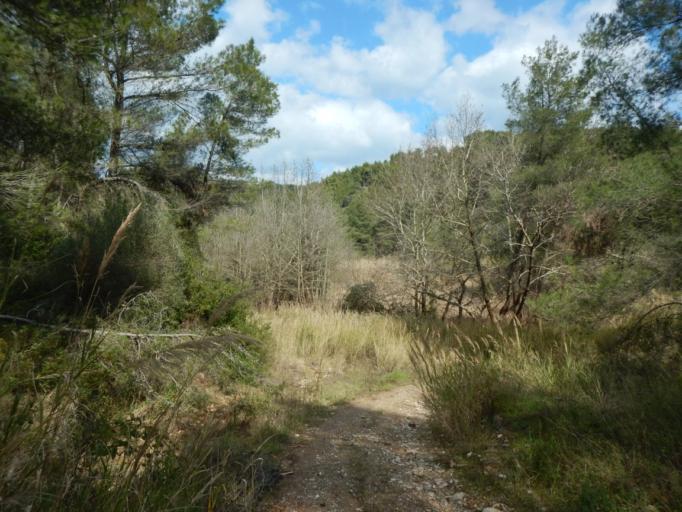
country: GR
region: Attica
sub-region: Nomarchia Anatolikis Attikis
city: Markopoulo Oropou
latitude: 38.2983
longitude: 23.8266
